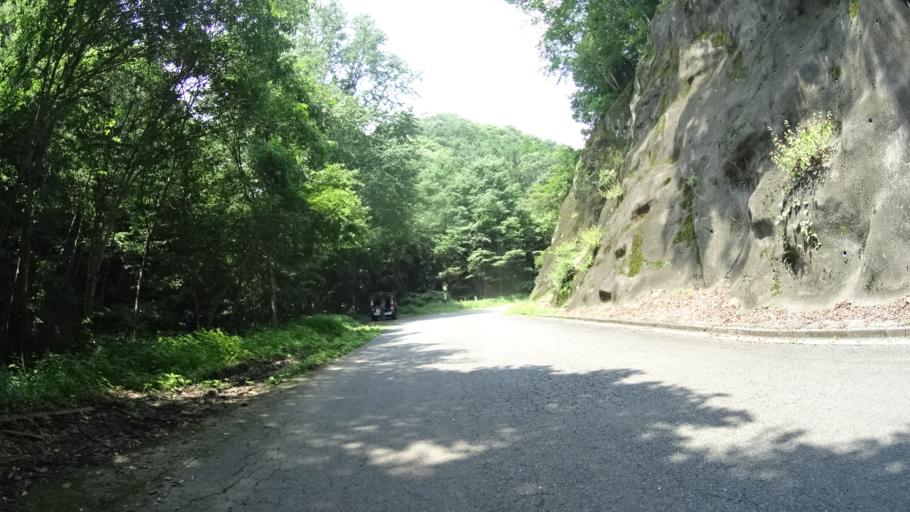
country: JP
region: Gunma
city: Tomioka
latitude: 36.0858
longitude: 138.7072
